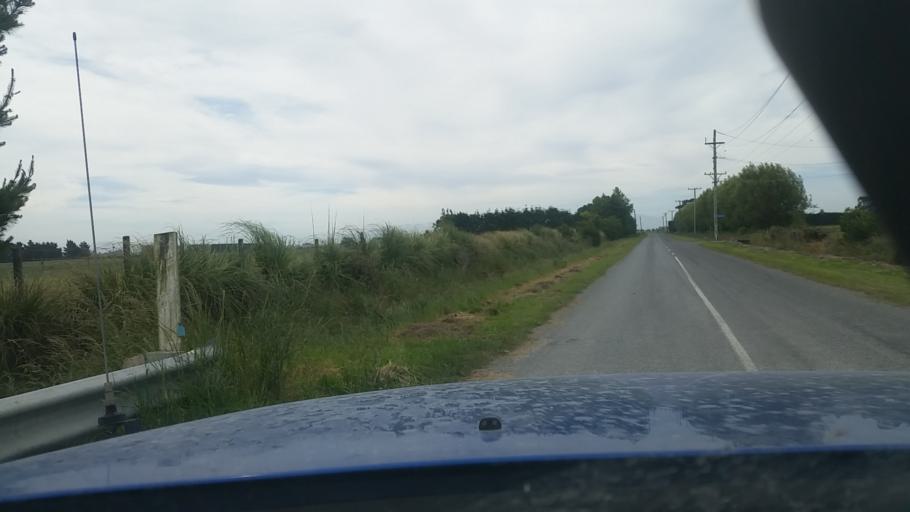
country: NZ
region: Canterbury
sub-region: Ashburton District
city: Tinwald
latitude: -44.0072
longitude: 171.7706
